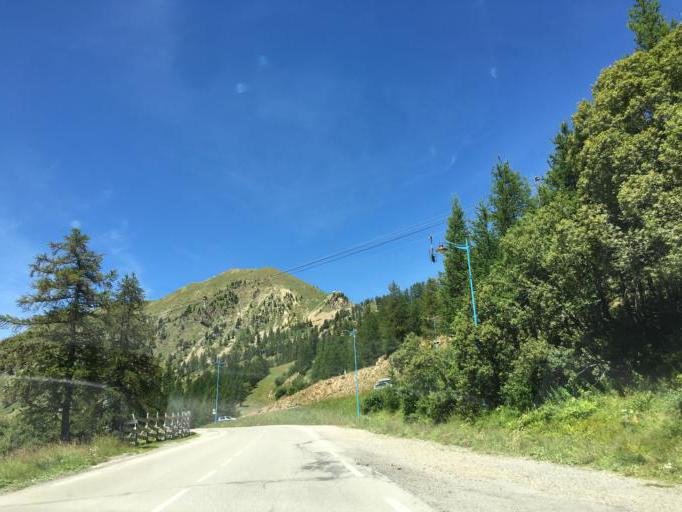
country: IT
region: Piedmont
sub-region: Provincia di Cuneo
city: Vinadio
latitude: 44.1893
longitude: 7.1562
